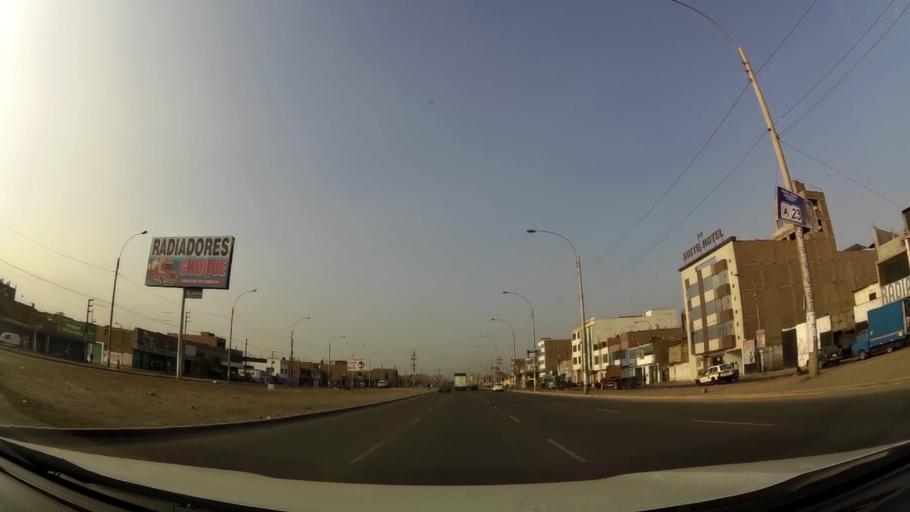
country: PE
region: Lima
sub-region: Lima
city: Independencia
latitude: -11.9878
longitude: -77.1037
